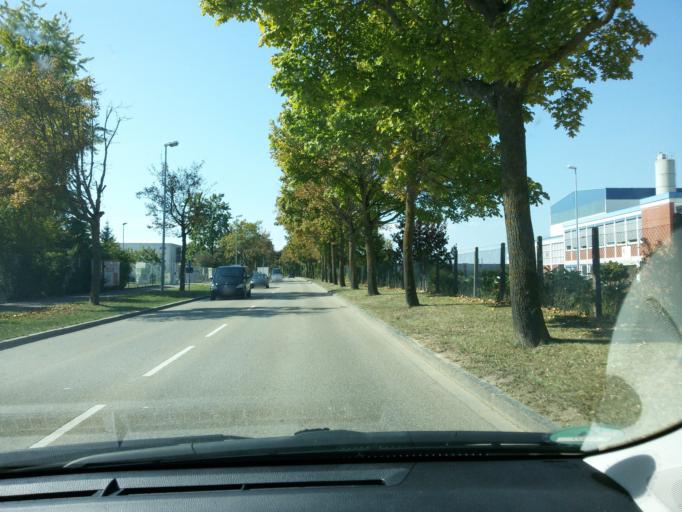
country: DE
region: Bavaria
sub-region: Swabia
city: Noerdlingen
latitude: 48.8645
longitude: 10.5114
